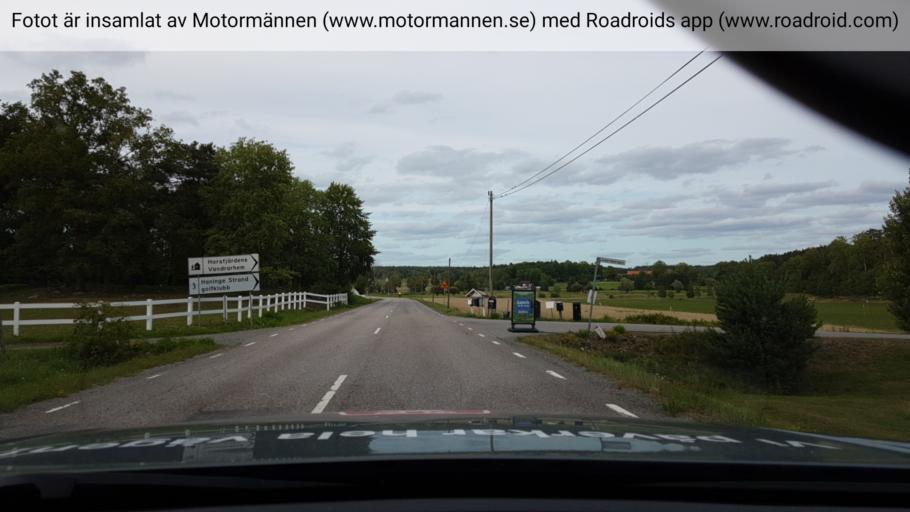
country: SE
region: Stockholm
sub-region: Haninge Kommun
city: Haninge
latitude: 59.1000
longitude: 18.1844
